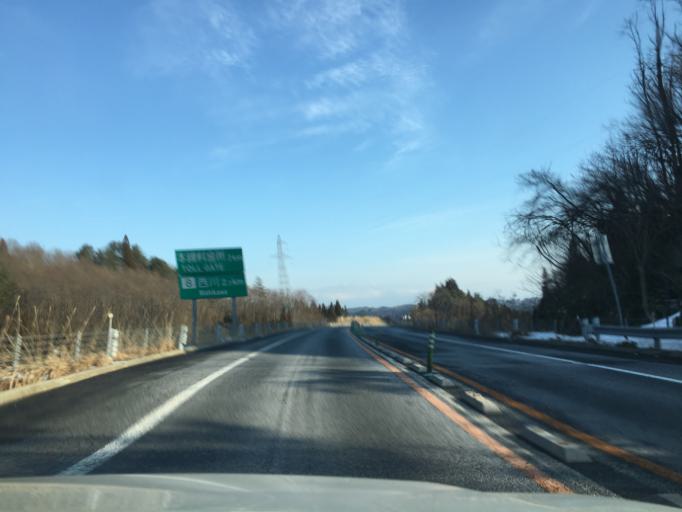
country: JP
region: Yamagata
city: Sagae
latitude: 38.4338
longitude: 140.1441
